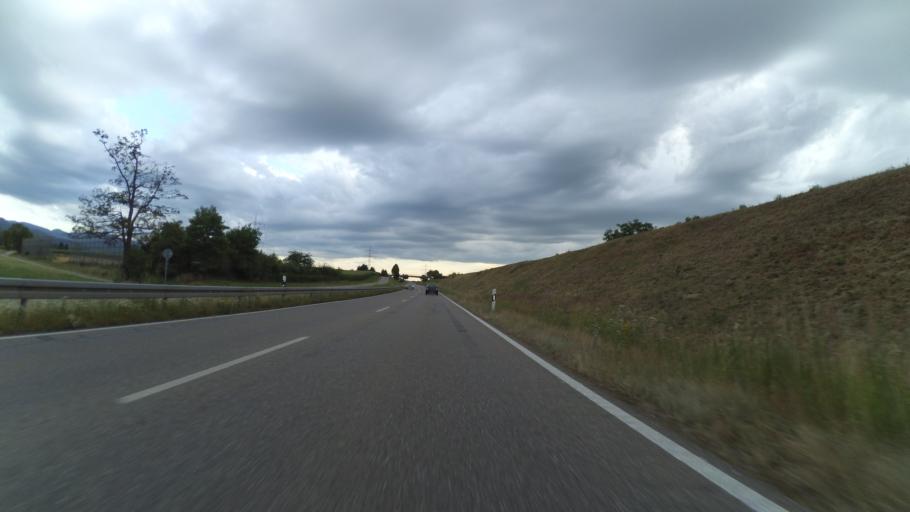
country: DE
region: Baden-Wuerttemberg
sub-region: Freiburg Region
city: Bad Krozingen
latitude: 47.9023
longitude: 7.7092
